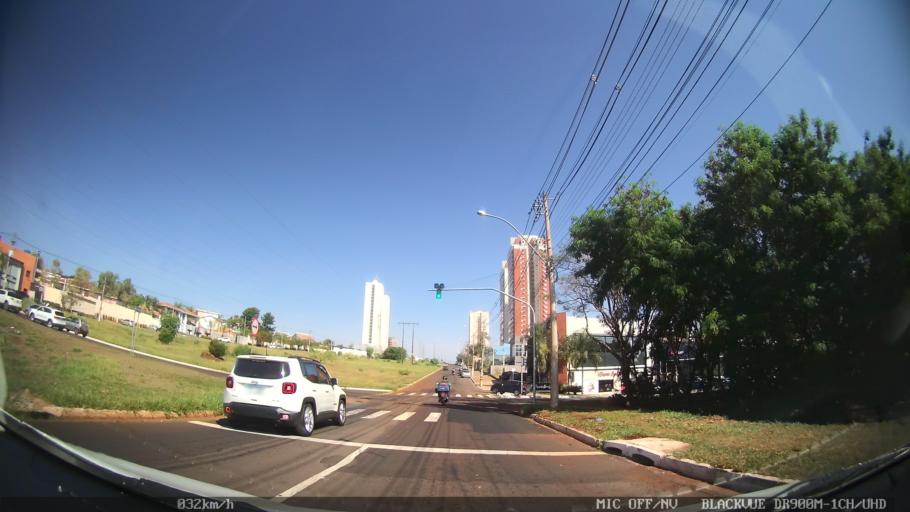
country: BR
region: Sao Paulo
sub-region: Ribeirao Preto
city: Ribeirao Preto
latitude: -21.2184
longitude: -47.7922
